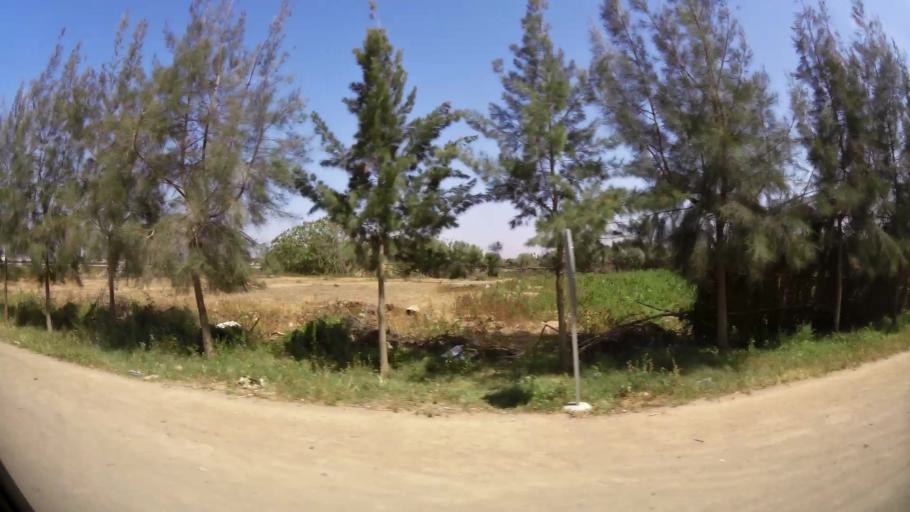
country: MA
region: Souss-Massa-Draa
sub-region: Inezgane-Ait Mellou
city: Inezgane
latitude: 30.3497
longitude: -9.5322
